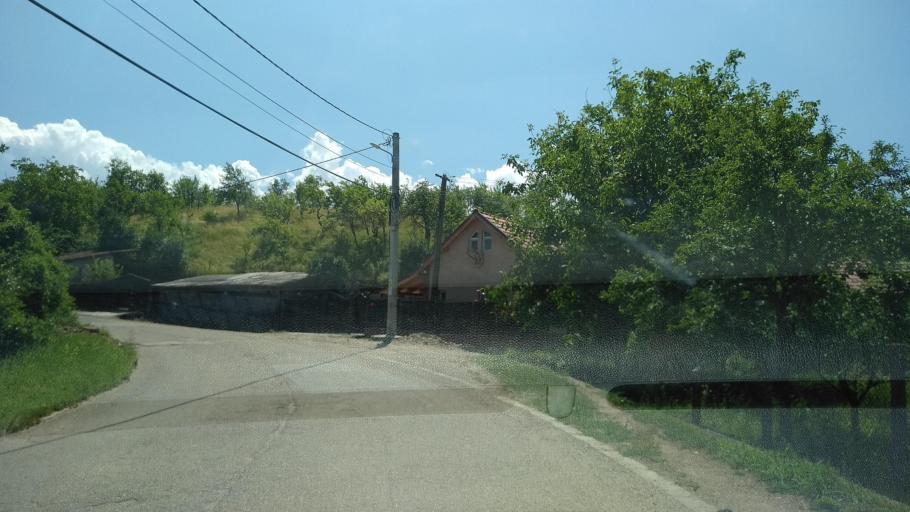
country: RO
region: Hunedoara
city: Densus
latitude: 45.5780
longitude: 22.8063
